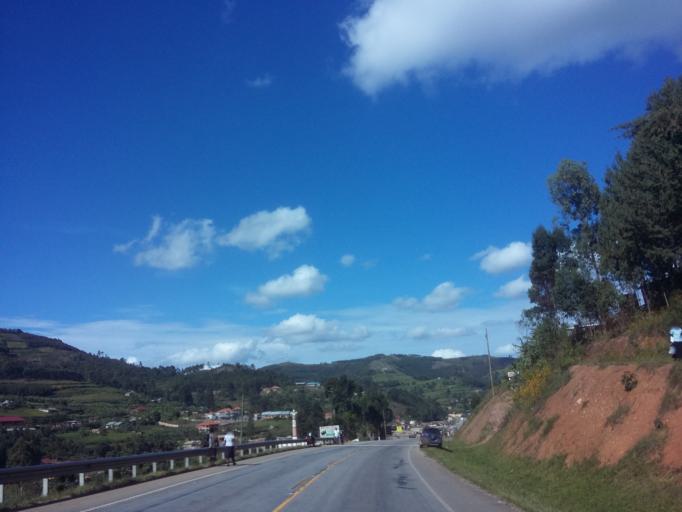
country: UG
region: Western Region
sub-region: Kabale District
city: Kabale
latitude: -1.1712
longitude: 30.1172
